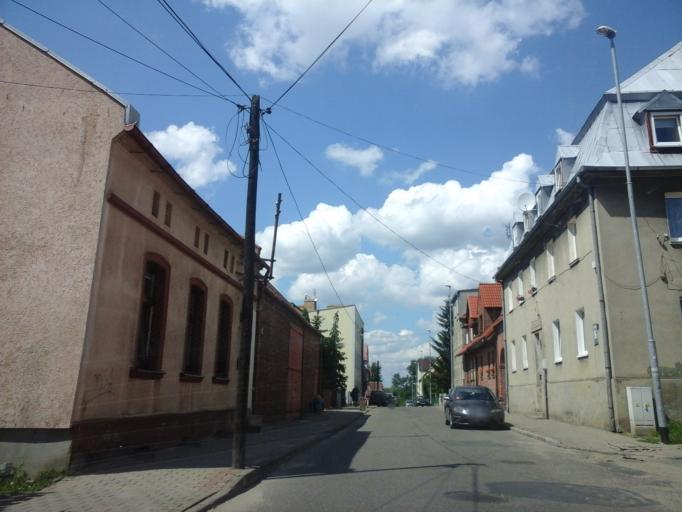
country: PL
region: West Pomeranian Voivodeship
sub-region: Powiat choszczenski
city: Choszczno
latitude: 53.1678
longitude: 15.4063
